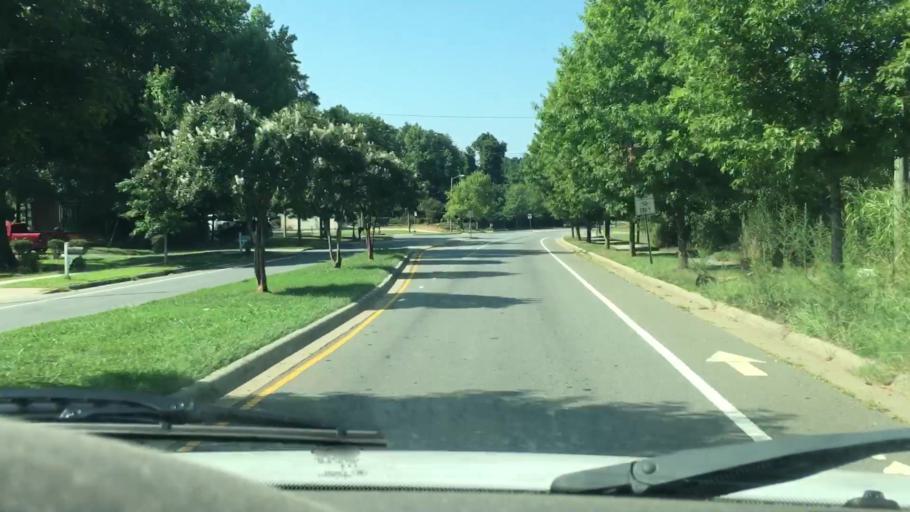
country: US
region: North Carolina
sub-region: Mecklenburg County
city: Charlotte
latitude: 35.2212
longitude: -80.9140
